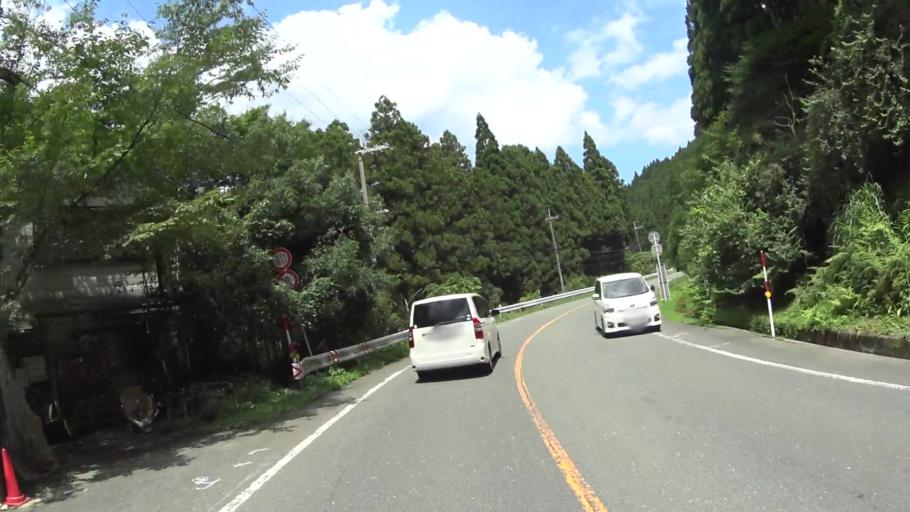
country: JP
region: Shiga Prefecture
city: Kitahama
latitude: 35.2762
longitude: 135.8785
